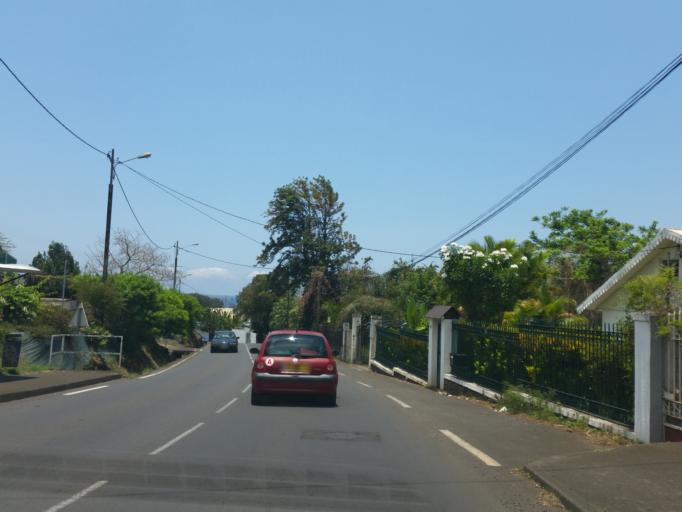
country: RE
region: Reunion
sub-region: Reunion
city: Sainte-Marie
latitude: -20.9074
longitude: 55.5038
